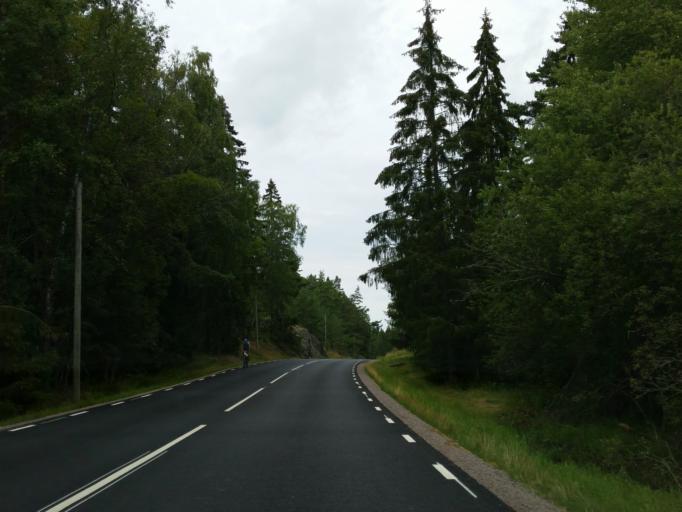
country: SE
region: Soedermanland
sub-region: Strangnas Kommun
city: Mariefred
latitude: 59.2666
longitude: 17.1604
